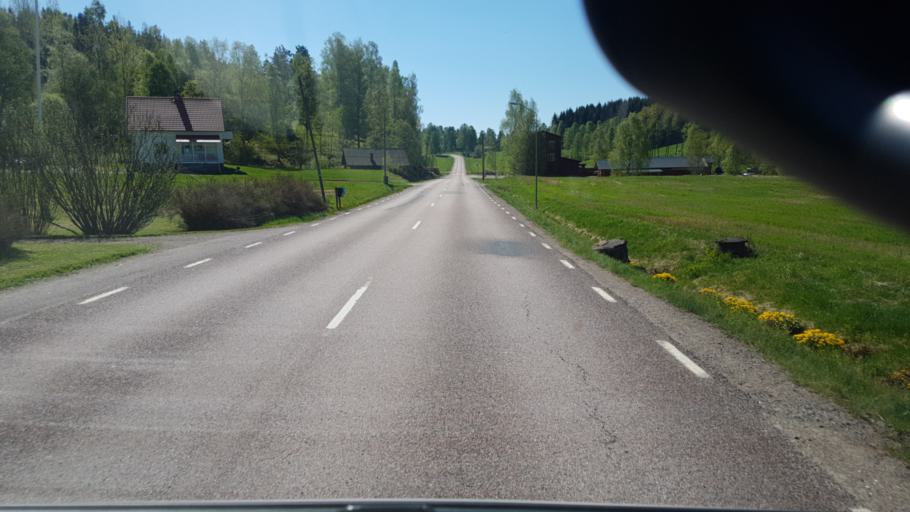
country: SE
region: Vaermland
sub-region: Arvika Kommun
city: Arvika
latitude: 59.8547
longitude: 12.5497
